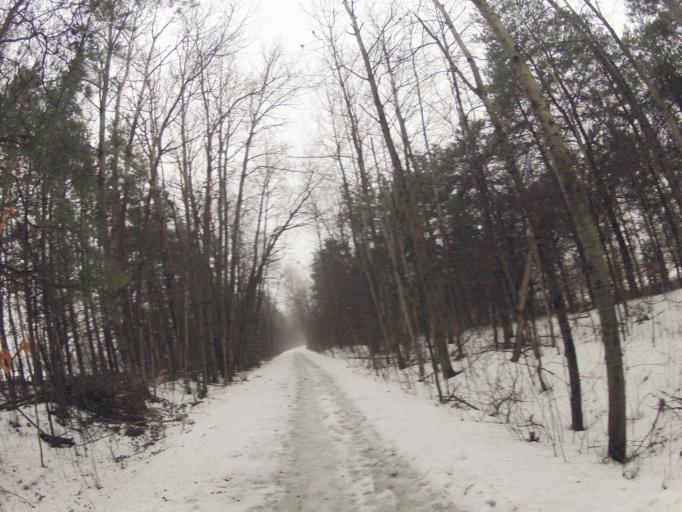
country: CA
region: Ontario
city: Brampton
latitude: 43.8380
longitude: -79.8899
